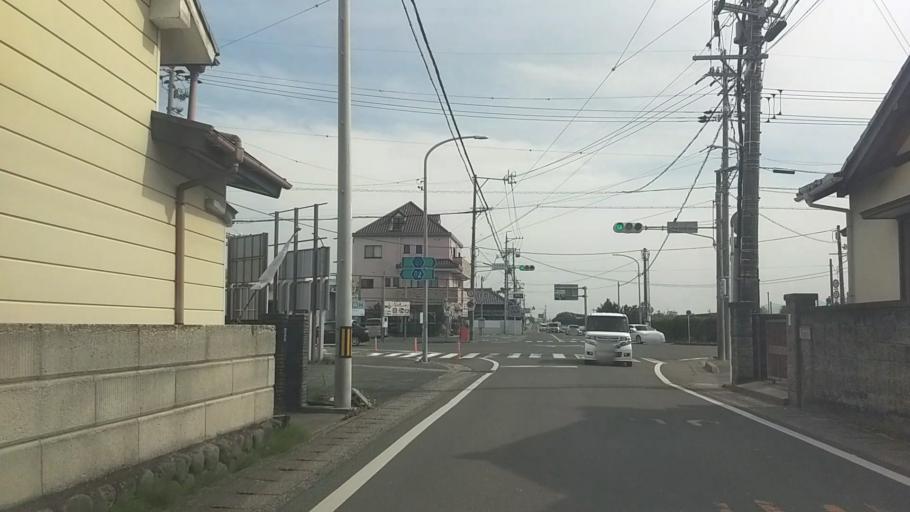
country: JP
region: Shizuoka
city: Kosai-shi
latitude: 34.6960
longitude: 137.6302
